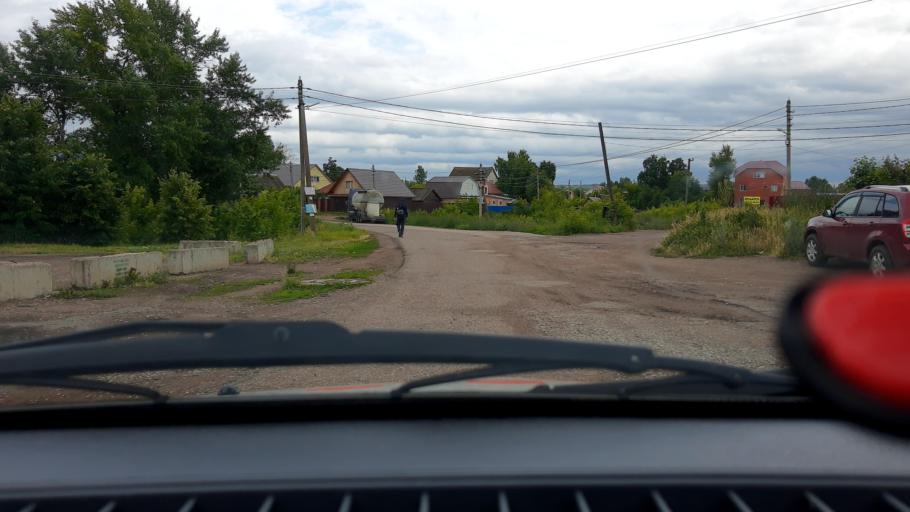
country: RU
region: Bashkortostan
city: Avdon
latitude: 54.4979
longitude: 55.8899
